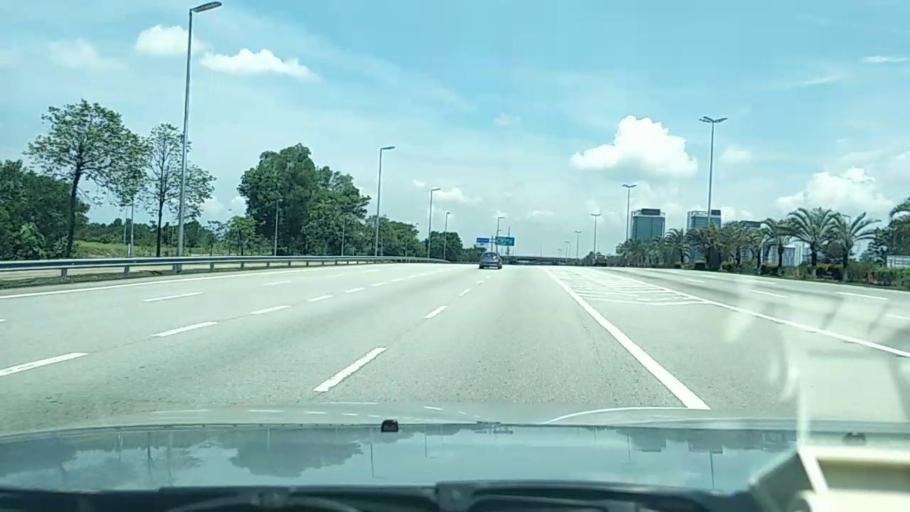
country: MY
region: Putrajaya
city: Putrajaya
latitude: 2.9330
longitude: 101.6676
